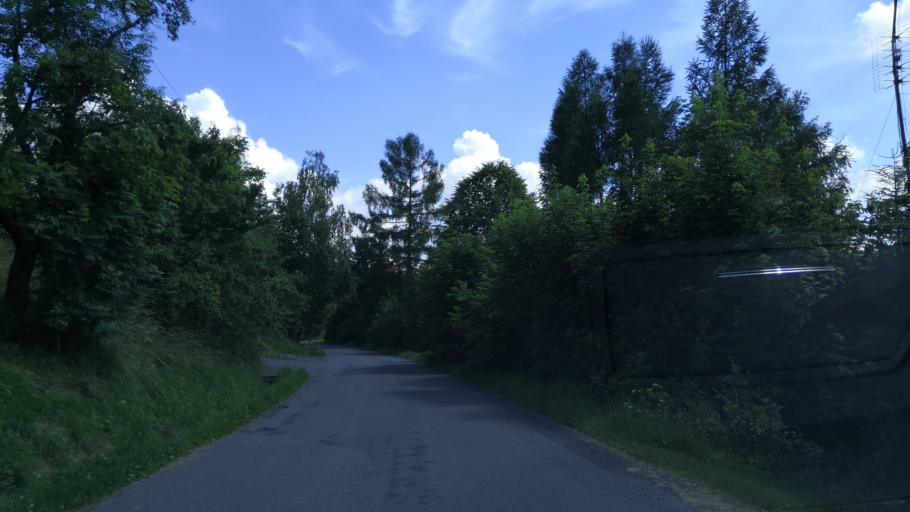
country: CZ
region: Zlin
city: Valasska Bystrice
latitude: 49.4286
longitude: 18.1111
